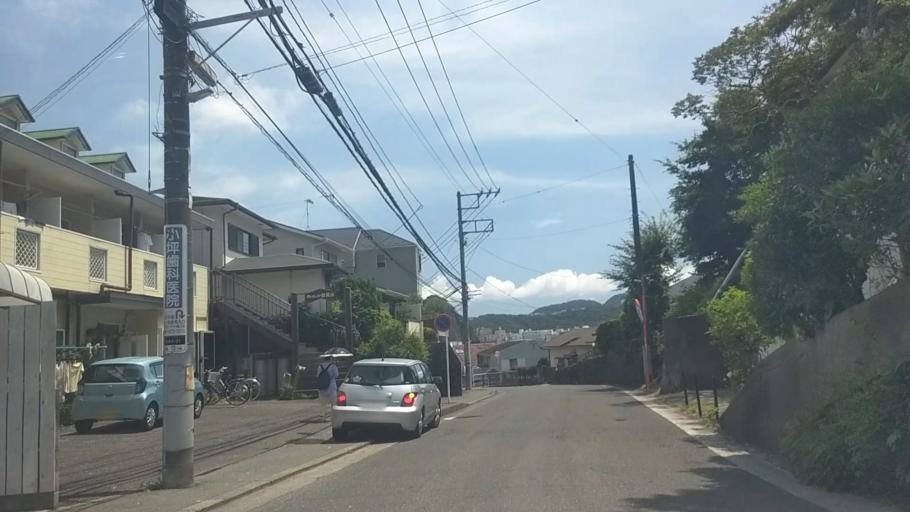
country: JP
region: Kanagawa
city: Zushi
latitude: 35.3004
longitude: 139.5681
